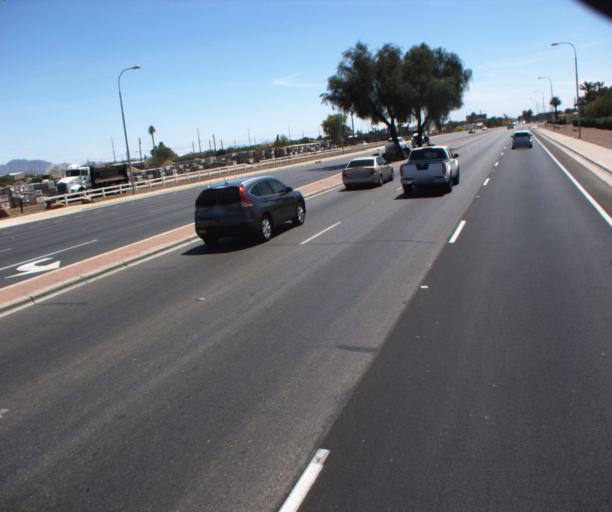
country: US
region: Arizona
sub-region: Maricopa County
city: Chandler
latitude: 33.2836
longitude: -111.8416
